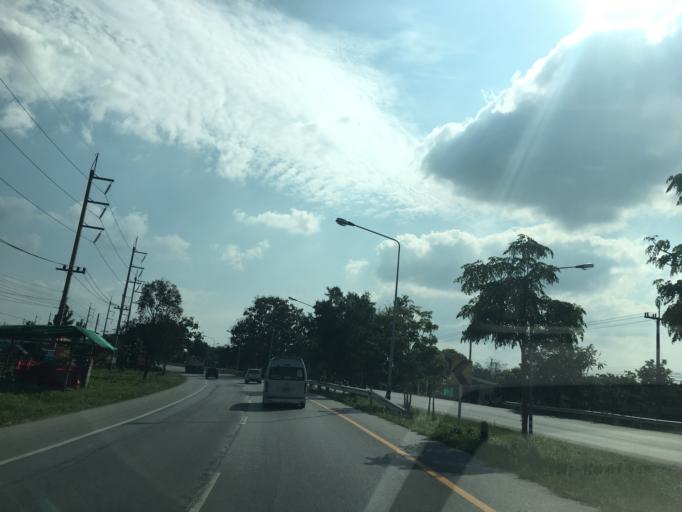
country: TH
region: Chiang Rai
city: Mae Lao
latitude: 19.7062
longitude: 99.7192
